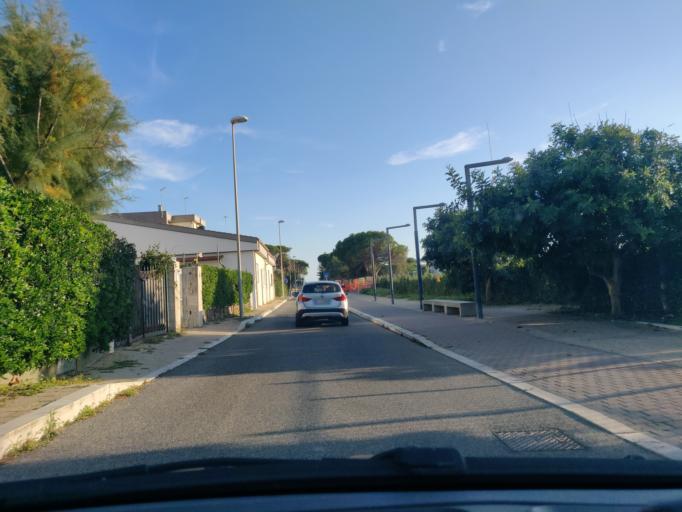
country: IT
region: Latium
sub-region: Citta metropolitana di Roma Capitale
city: Santa Marinella
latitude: 42.0342
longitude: 11.8334
